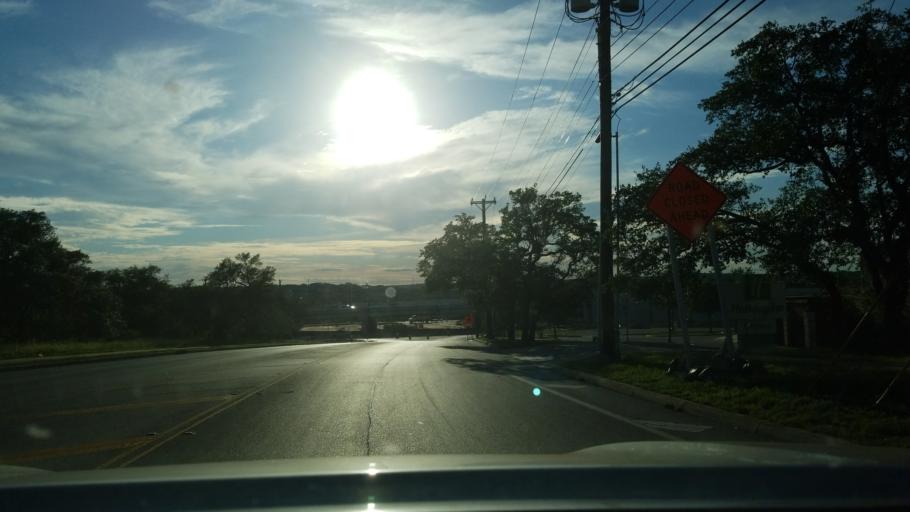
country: US
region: Texas
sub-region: Bexar County
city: Hollywood Park
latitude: 29.6207
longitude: -98.4624
